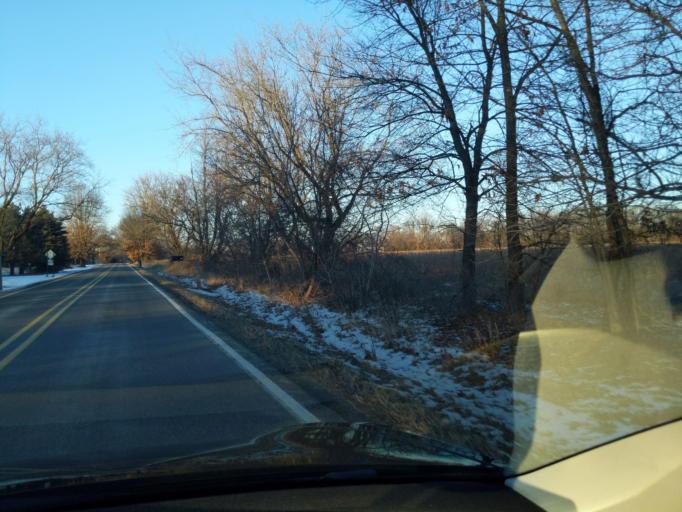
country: US
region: Michigan
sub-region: Ingham County
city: Stockbridge
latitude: 42.4879
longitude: -84.2178
